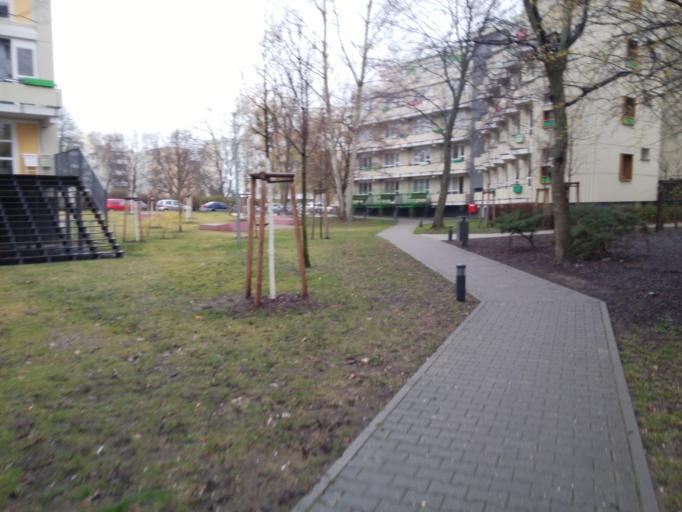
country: DE
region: Berlin
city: Hansaviertel
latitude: 52.5167
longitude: 13.3363
